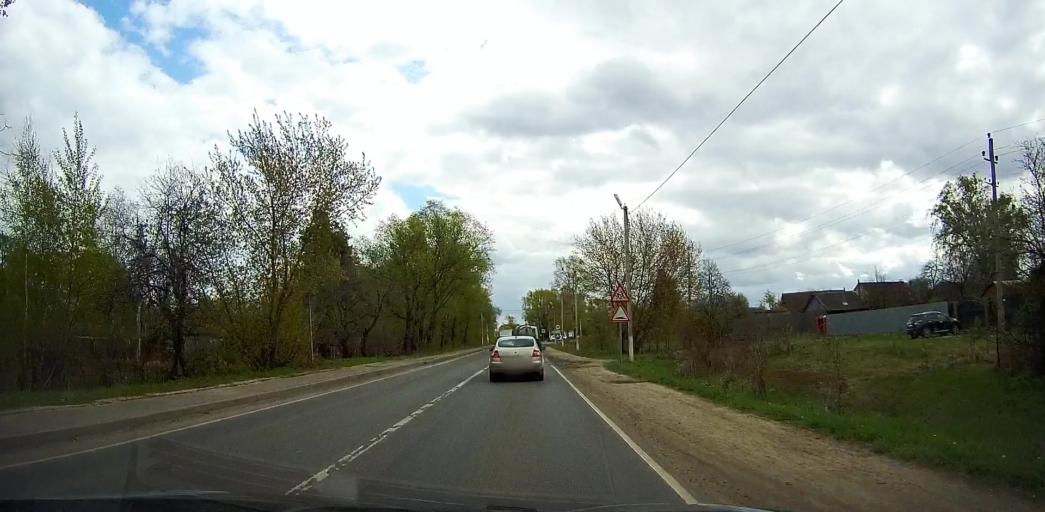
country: RU
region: Moskovskaya
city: Beloozerskiy
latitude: 55.4455
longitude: 38.4929
